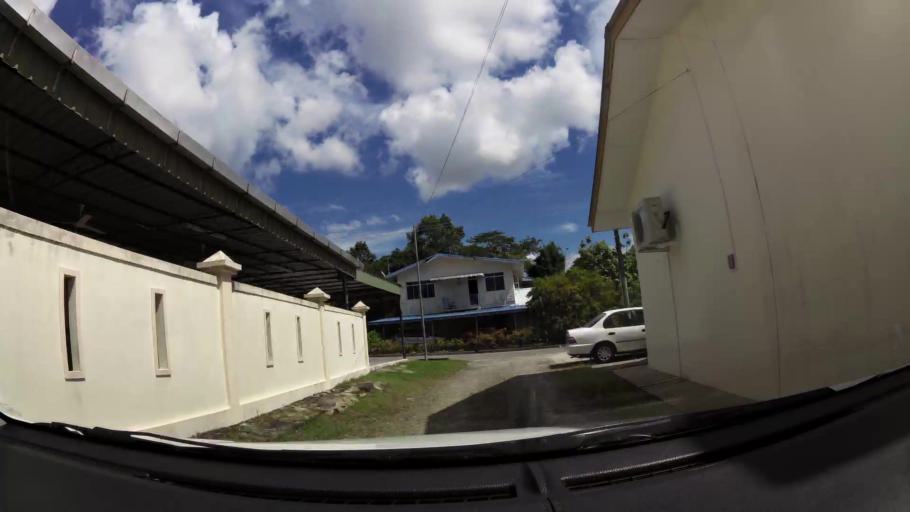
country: BN
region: Brunei and Muara
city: Bandar Seri Begawan
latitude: 4.9676
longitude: 114.9444
